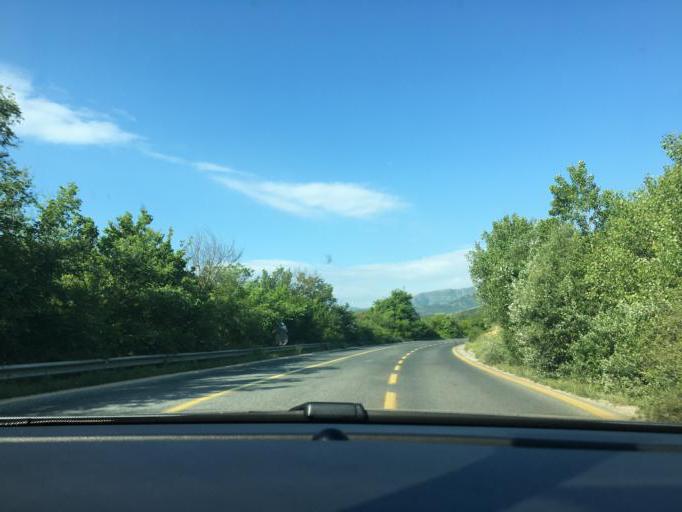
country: MK
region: Rosoman
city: Rosoman
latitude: 41.4249
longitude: 21.8023
